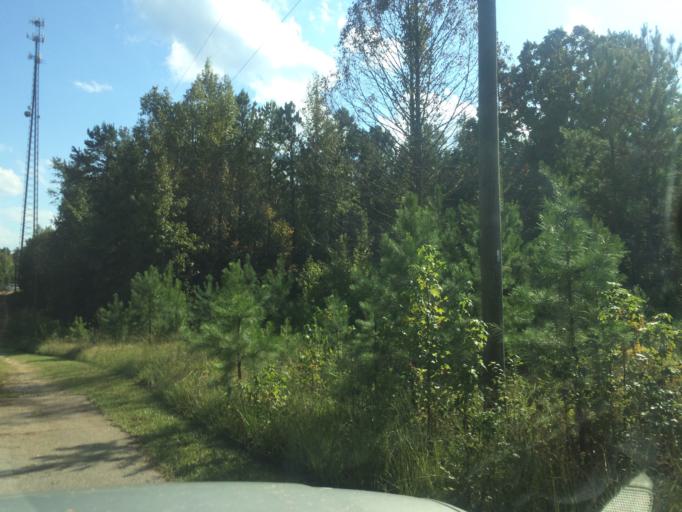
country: US
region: South Carolina
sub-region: Greenwood County
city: Ware Shoals
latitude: 34.4634
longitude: -82.1714
